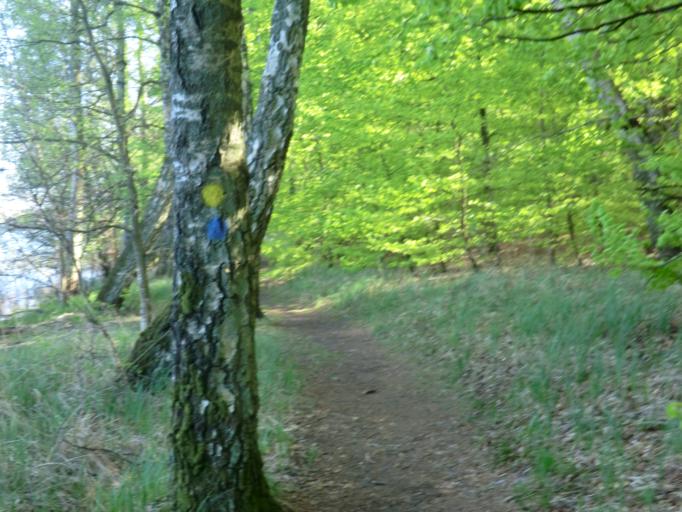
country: SE
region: Skane
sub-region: Sjobo Kommun
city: Sjoebo
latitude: 55.5707
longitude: 13.7183
